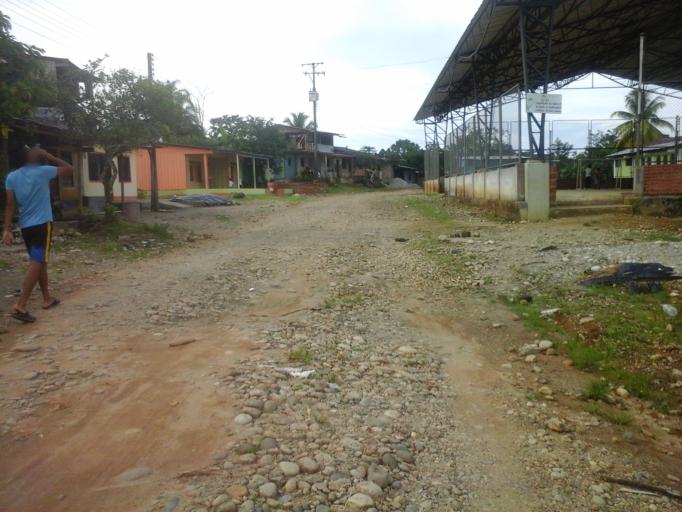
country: CO
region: Putumayo
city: Orito
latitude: 0.6485
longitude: -76.8246
